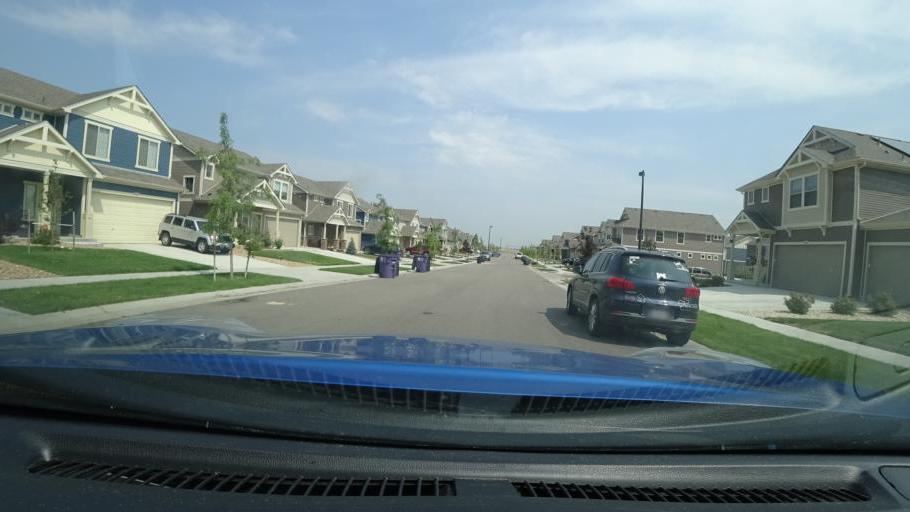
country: US
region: Colorado
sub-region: Adams County
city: Aurora
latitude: 39.7772
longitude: -104.7817
